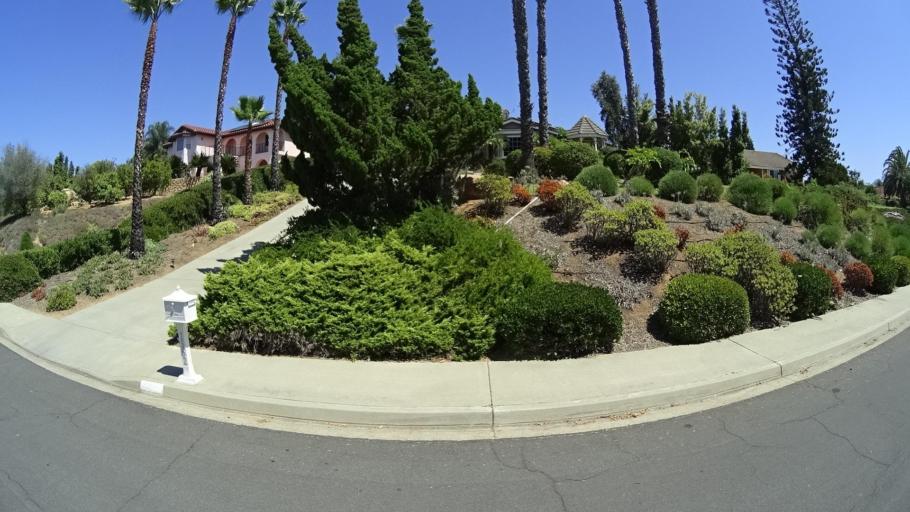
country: US
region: California
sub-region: San Diego County
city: Fallbrook
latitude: 33.3646
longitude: -117.2568
